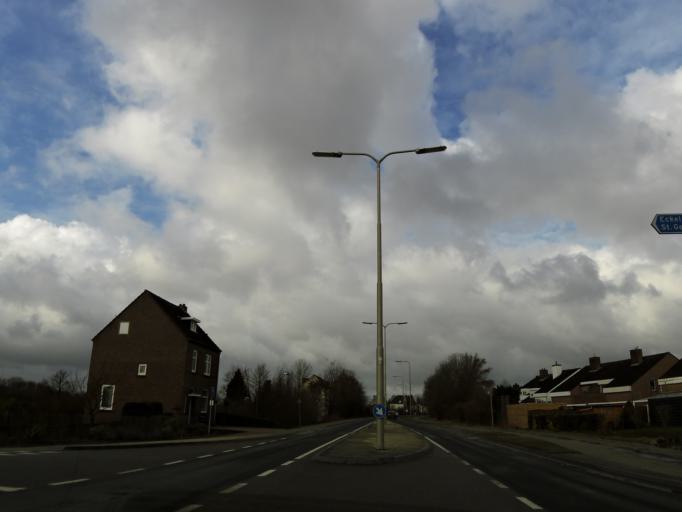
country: NL
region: Limburg
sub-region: Gemeente Maastricht
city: Heer
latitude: 50.8264
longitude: 5.7668
